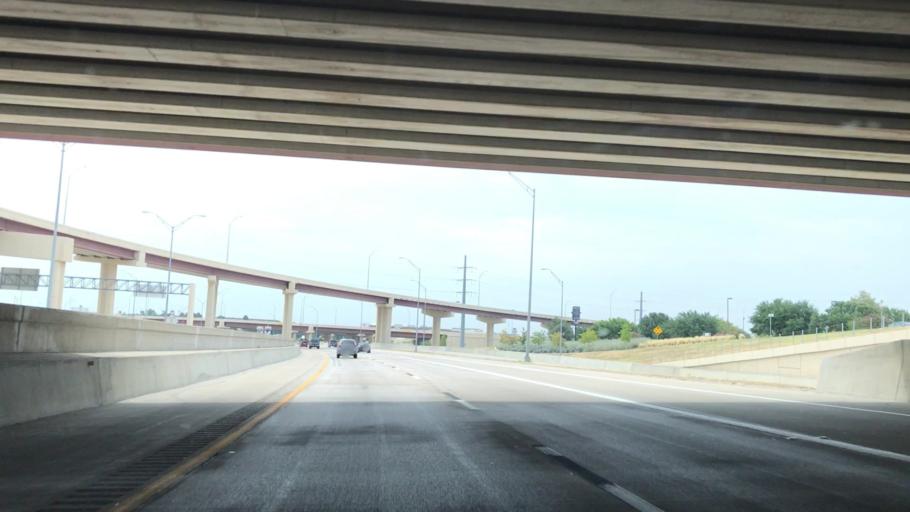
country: US
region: Texas
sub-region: Tarrant County
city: Grapevine
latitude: 32.9250
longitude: -97.0886
